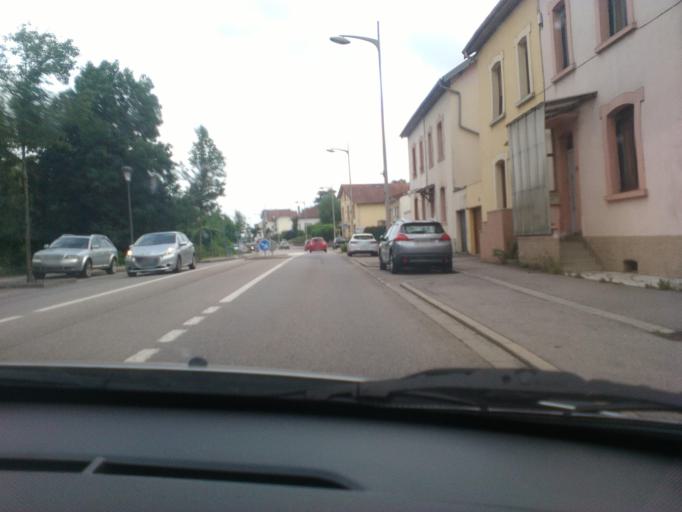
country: FR
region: Lorraine
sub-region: Departement de Meurthe-et-Moselle
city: Frouard
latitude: 48.7505
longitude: 6.1464
